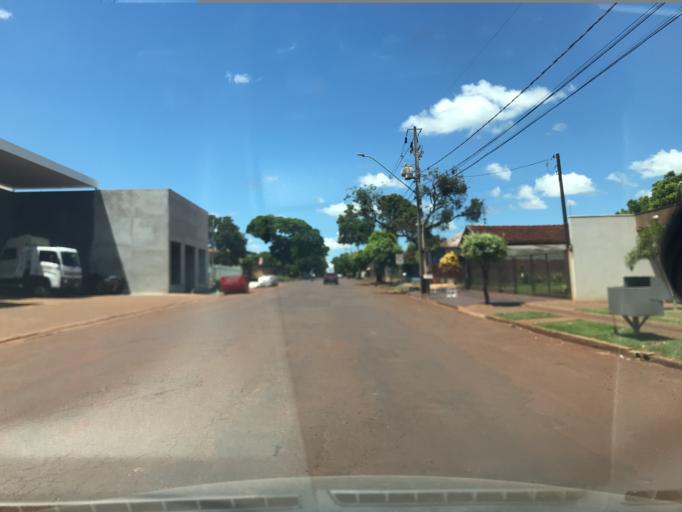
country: BR
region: Parana
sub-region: Palotina
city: Palotina
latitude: -24.2875
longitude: -53.8462
